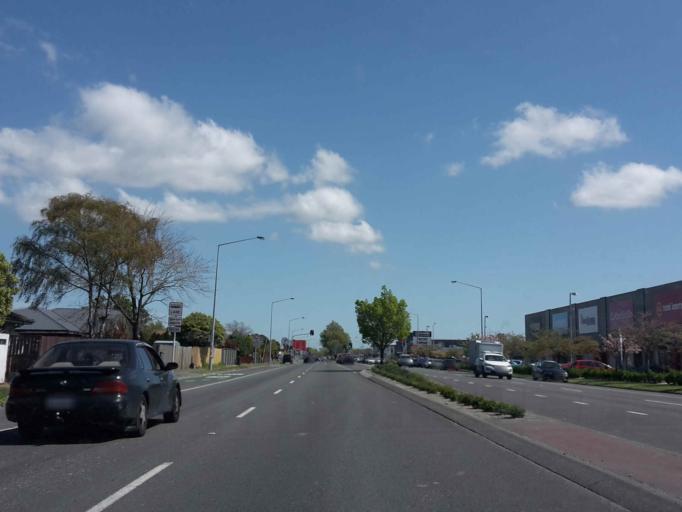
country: NZ
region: Canterbury
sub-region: Selwyn District
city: Prebbleton
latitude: -43.5429
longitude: 172.5322
